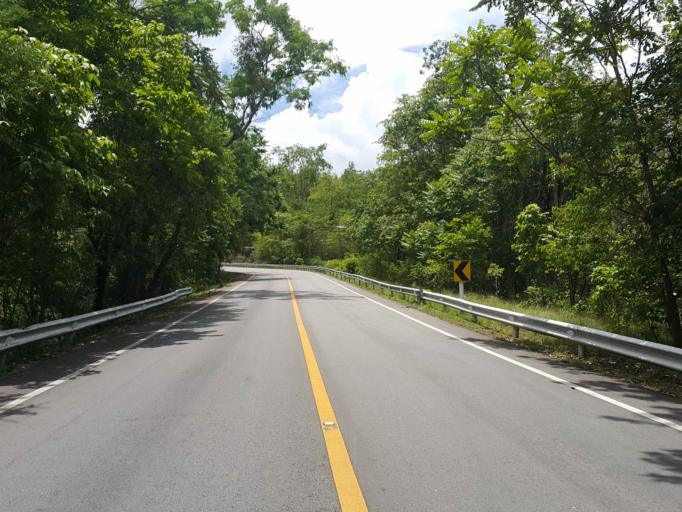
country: TH
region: Chiang Mai
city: Chom Thong
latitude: 18.4995
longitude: 98.6717
